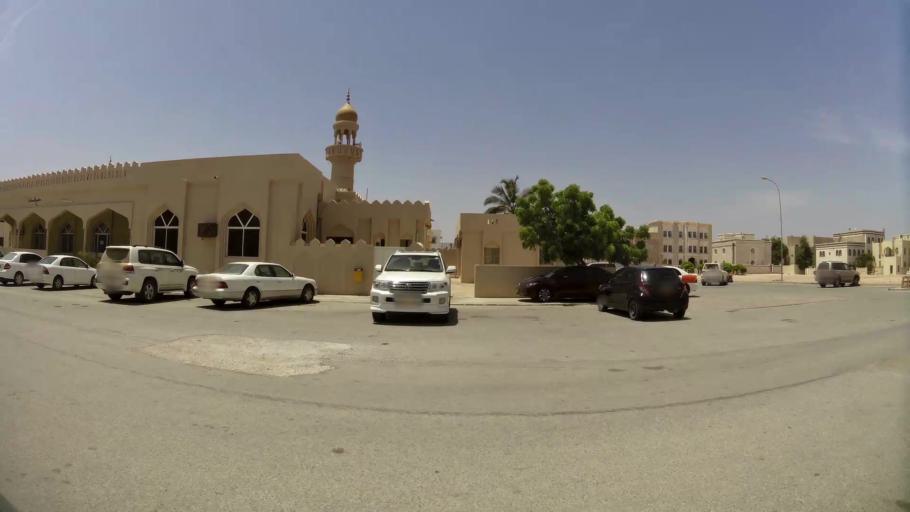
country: OM
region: Zufar
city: Salalah
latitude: 17.0665
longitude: 54.1516
